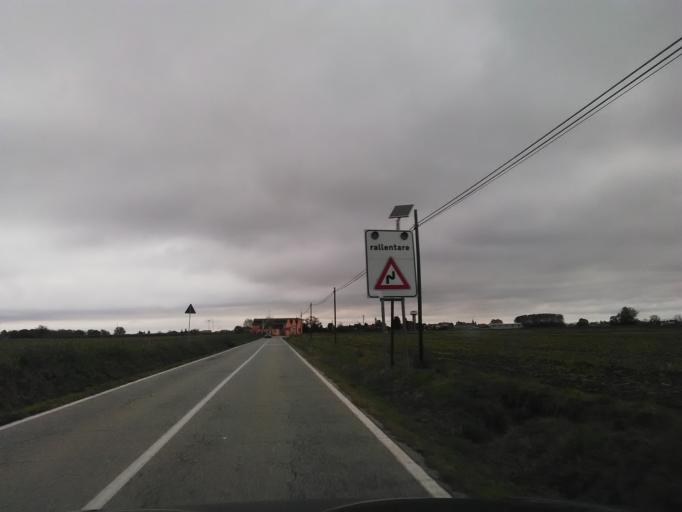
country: IT
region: Piedmont
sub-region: Provincia di Vercelli
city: Moncrivello
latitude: 45.3114
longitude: 7.9992
